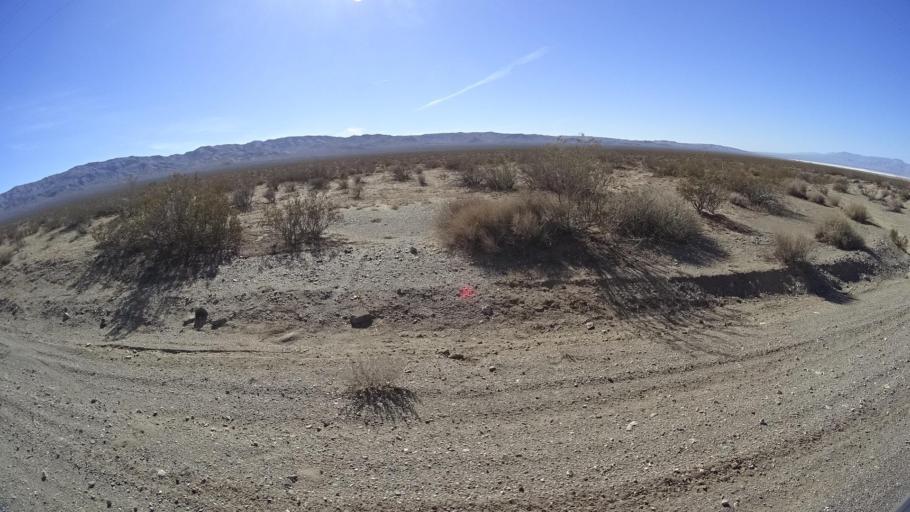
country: US
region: California
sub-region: Kern County
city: Ridgecrest
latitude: 35.3871
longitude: -117.7453
